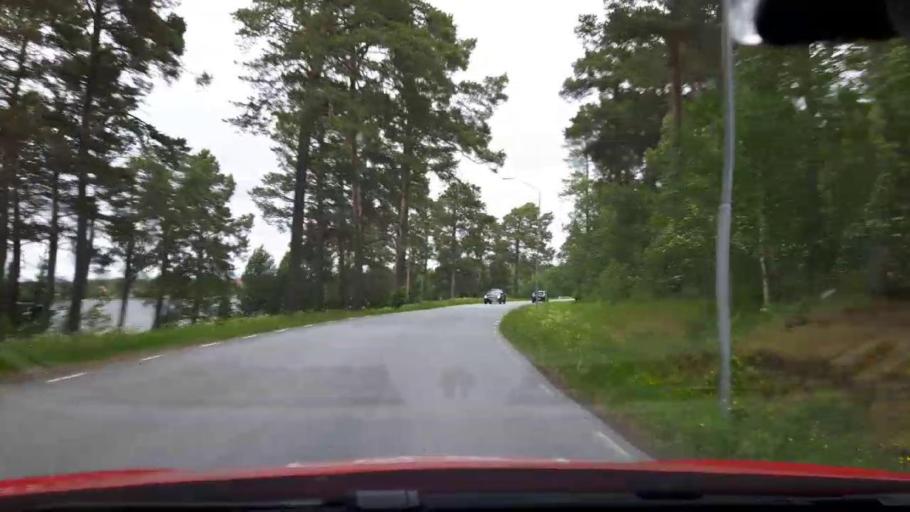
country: SE
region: Jaemtland
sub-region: OEstersunds Kommun
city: Ostersund
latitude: 63.1936
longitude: 14.6325
